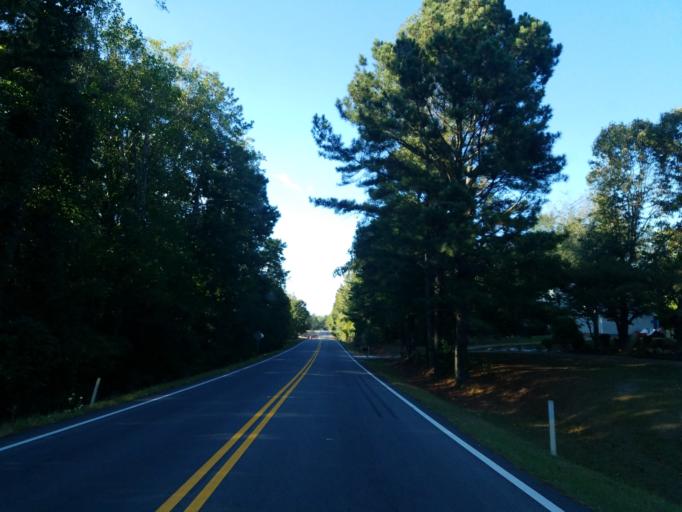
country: US
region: Georgia
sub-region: Bartow County
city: Emerson
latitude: 34.0669
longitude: -84.8265
